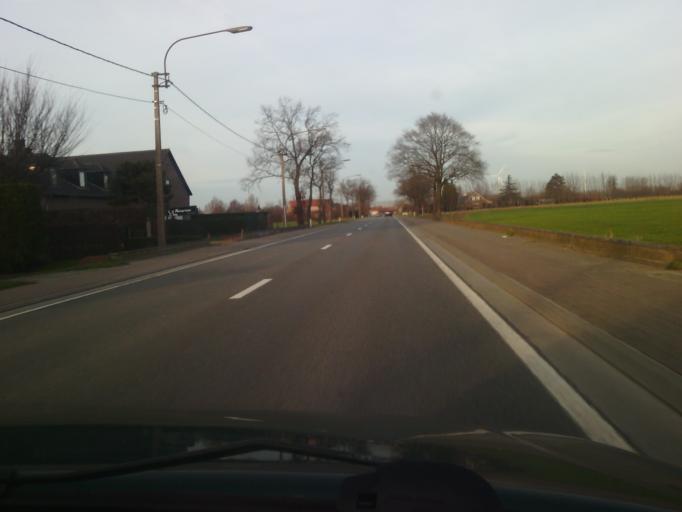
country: BE
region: Flanders
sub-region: Provincie Oost-Vlaanderen
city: Laarne
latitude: 51.0465
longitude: 3.8802
